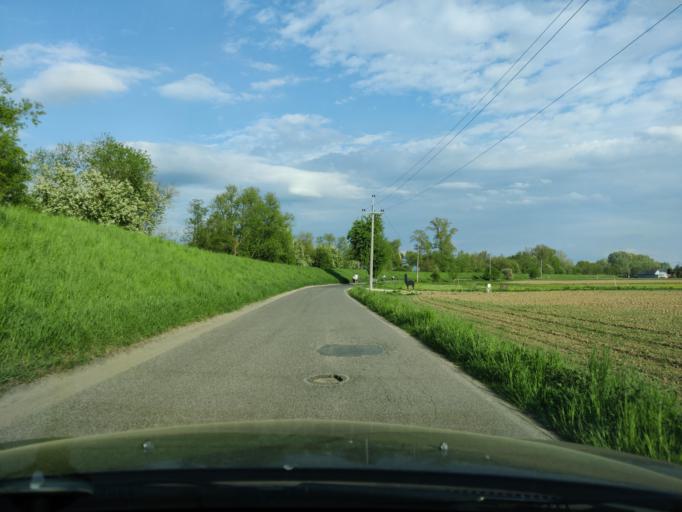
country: PL
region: Masovian Voivodeship
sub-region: Powiat otwocki
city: Jozefow
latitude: 52.1199
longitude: 21.1771
